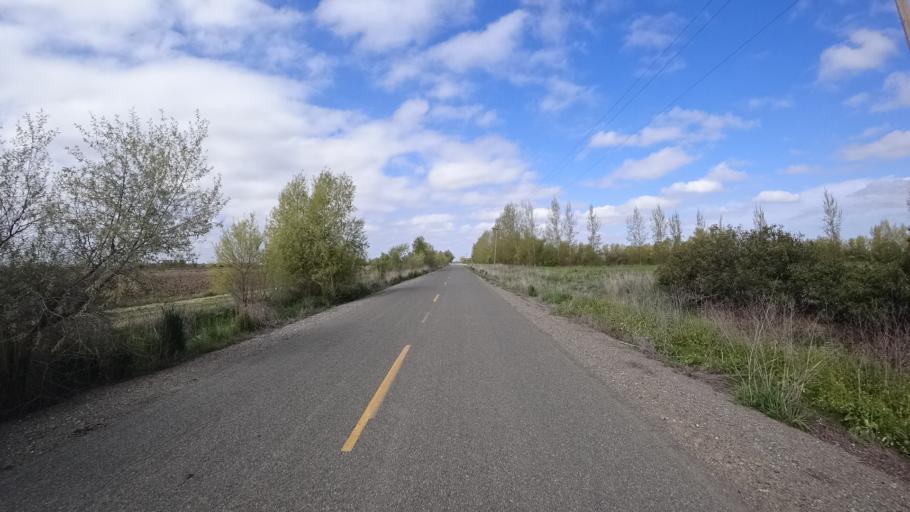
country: US
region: California
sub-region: Butte County
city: Biggs
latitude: 39.4203
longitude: -121.9125
